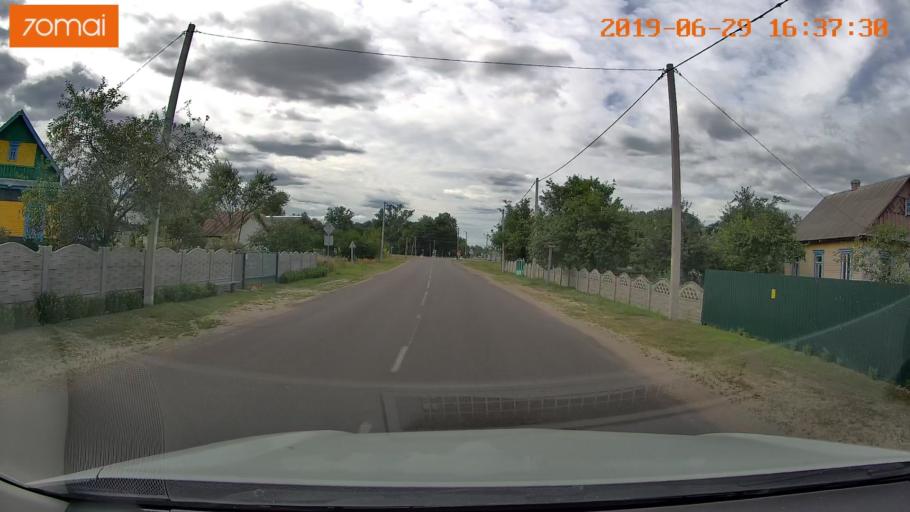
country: BY
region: Brest
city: Luninyets
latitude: 52.2279
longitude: 27.0214
